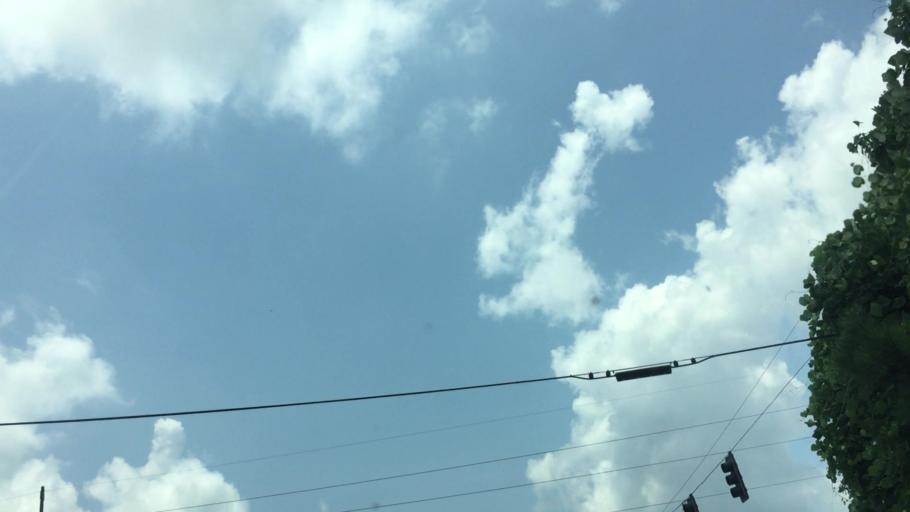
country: US
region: Georgia
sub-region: Carroll County
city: Carrollton
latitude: 33.6148
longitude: -84.9979
